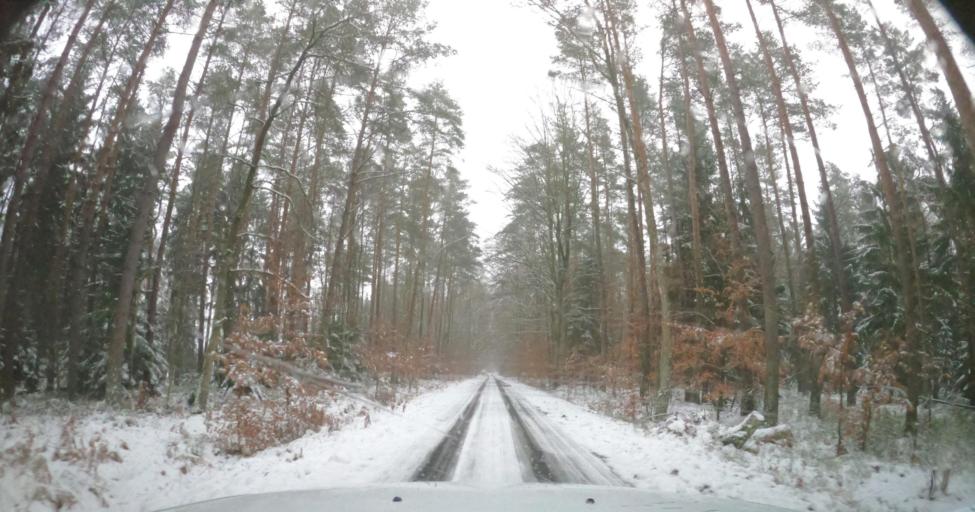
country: PL
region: West Pomeranian Voivodeship
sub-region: Powiat goleniowski
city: Przybiernow
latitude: 53.6617
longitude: 14.7815
